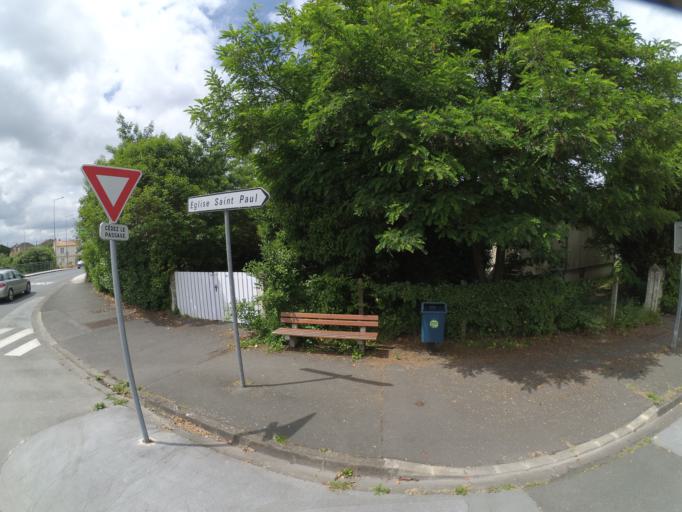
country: FR
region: Poitou-Charentes
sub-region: Departement de la Charente-Maritime
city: Rochefort
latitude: 45.9482
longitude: -0.9676
